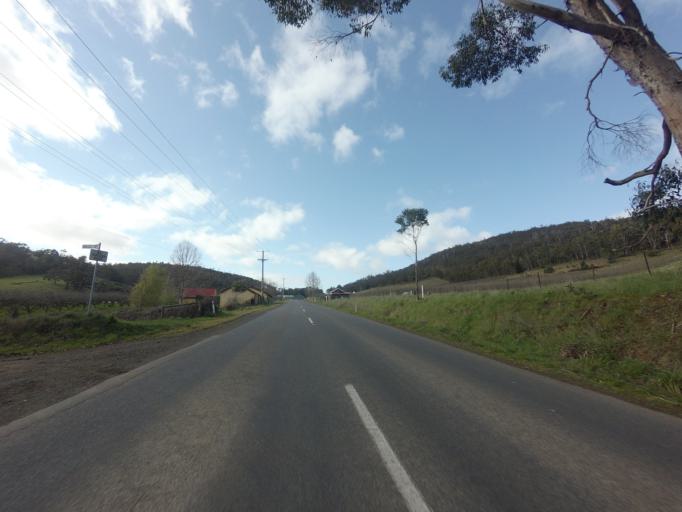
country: AU
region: Tasmania
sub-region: Huon Valley
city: Geeveston
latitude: -43.1704
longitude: 146.9426
